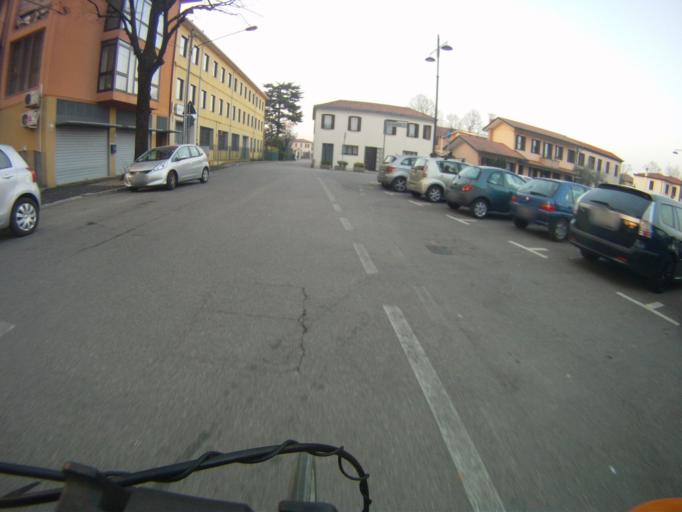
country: IT
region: Veneto
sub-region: Provincia di Padova
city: Ponte San Nicolo
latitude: 45.3787
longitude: 11.9020
